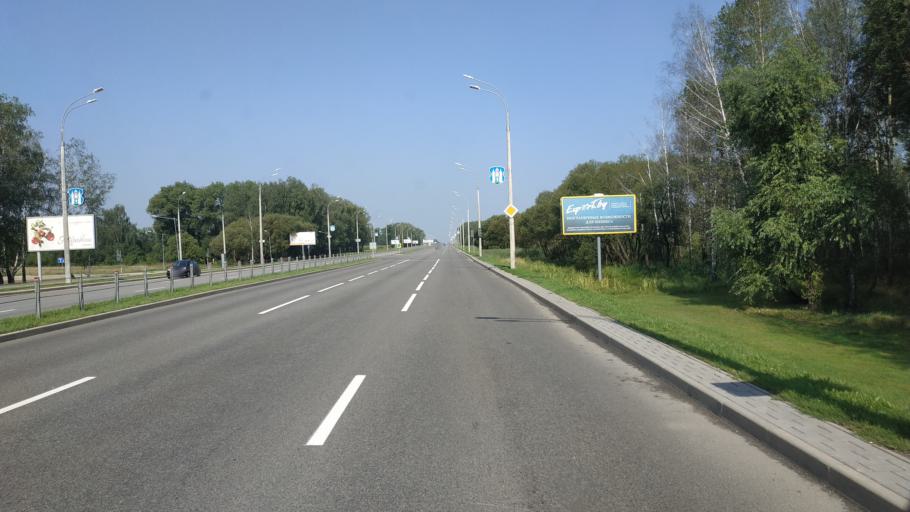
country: BY
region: Mogilev
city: Buynichy
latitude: 53.9388
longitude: 30.2452
